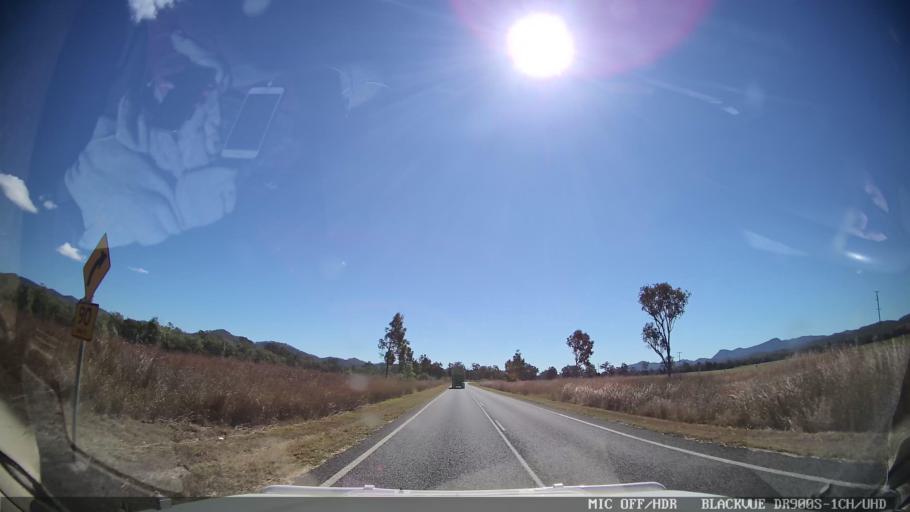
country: AU
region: Queensland
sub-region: Gladstone
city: Toolooa
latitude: -24.2795
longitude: 151.2778
